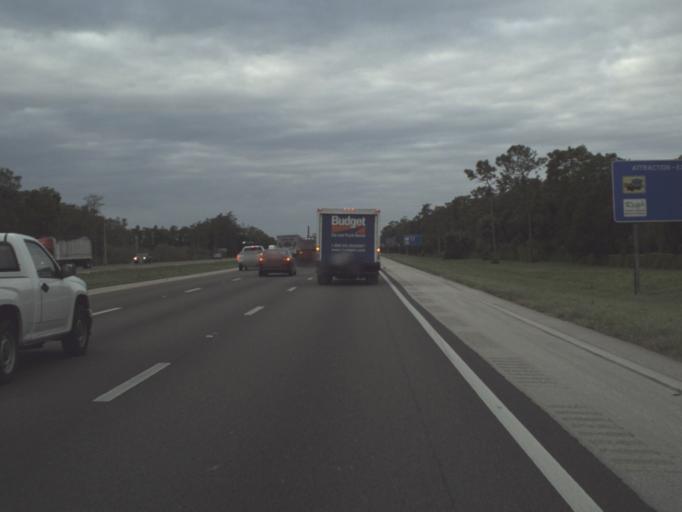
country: US
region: Florida
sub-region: Lee County
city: Bonita Springs
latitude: 26.2898
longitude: -81.7430
